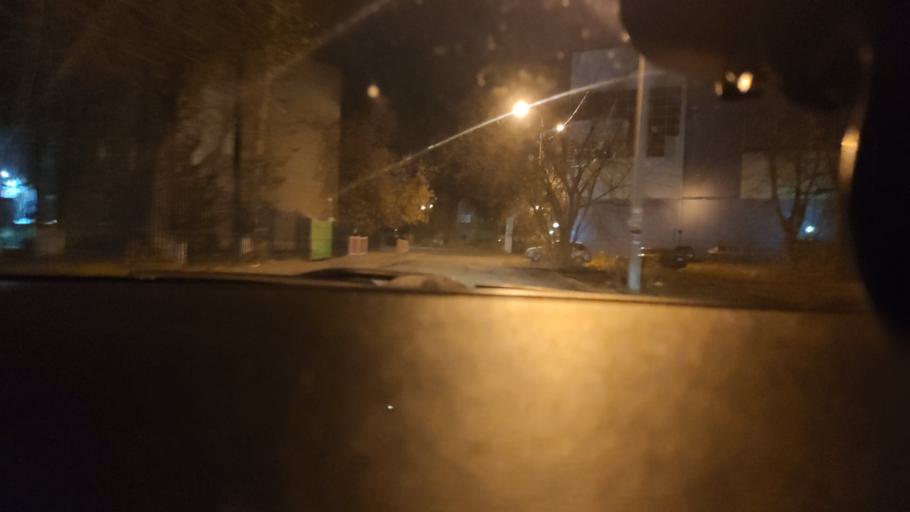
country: RU
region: Perm
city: Perm
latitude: 57.9738
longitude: 56.2416
